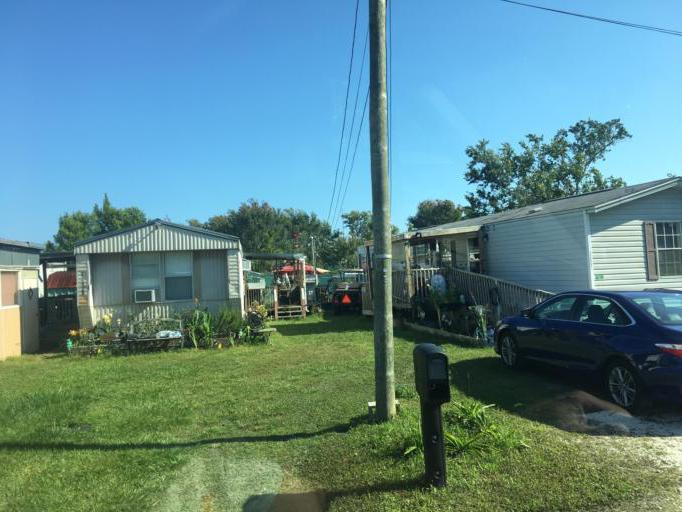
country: US
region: Florida
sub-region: Bay County
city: Panama City Beach
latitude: 30.2022
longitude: -85.8332
